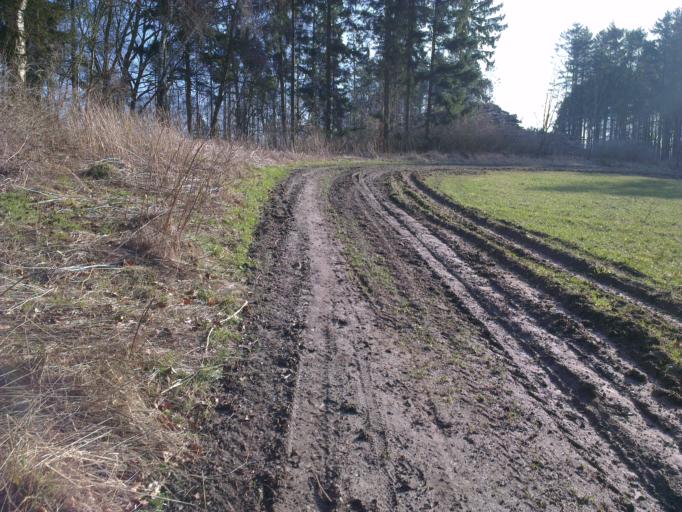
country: DK
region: Capital Region
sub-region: Frederikssund Kommune
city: Skibby
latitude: 55.7839
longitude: 11.9554
